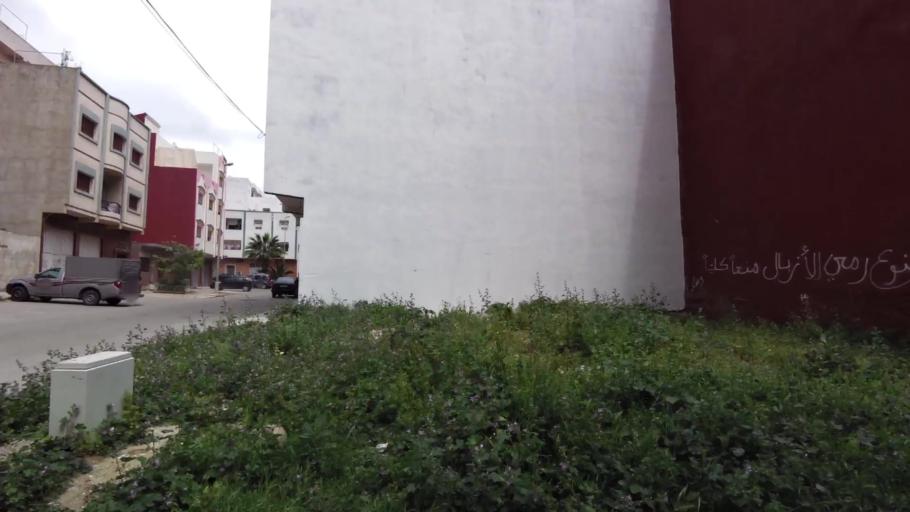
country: MA
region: Tanger-Tetouan
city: Tetouan
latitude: 35.5640
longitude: -5.3581
